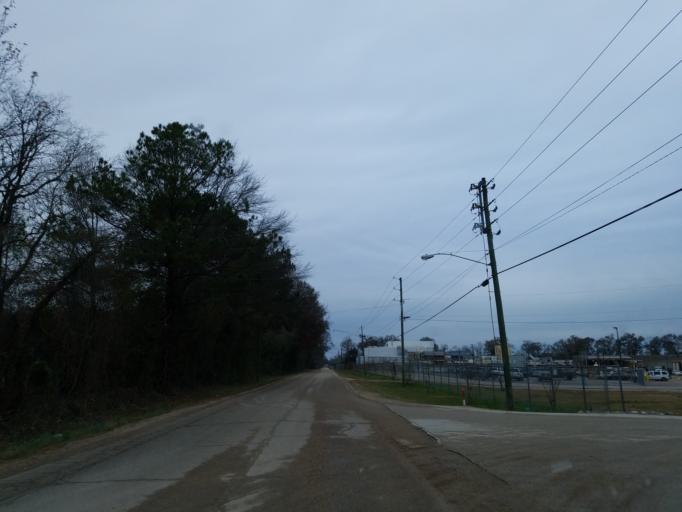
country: US
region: Mississippi
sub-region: Forrest County
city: Hattiesburg
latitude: 31.3033
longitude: -89.2771
